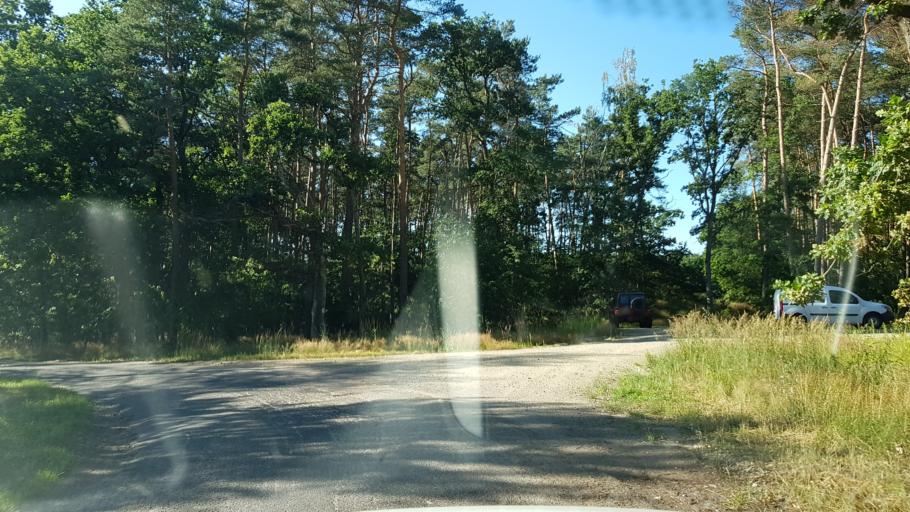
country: PL
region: West Pomeranian Voivodeship
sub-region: Powiat goleniowski
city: Goleniow
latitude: 53.5591
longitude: 14.7630
